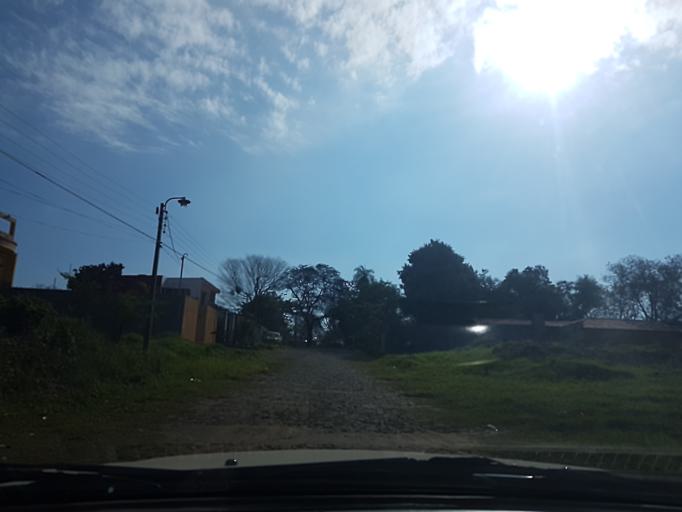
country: PY
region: Central
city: Colonia Mariano Roque Alonso
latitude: -25.2468
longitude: -57.5353
